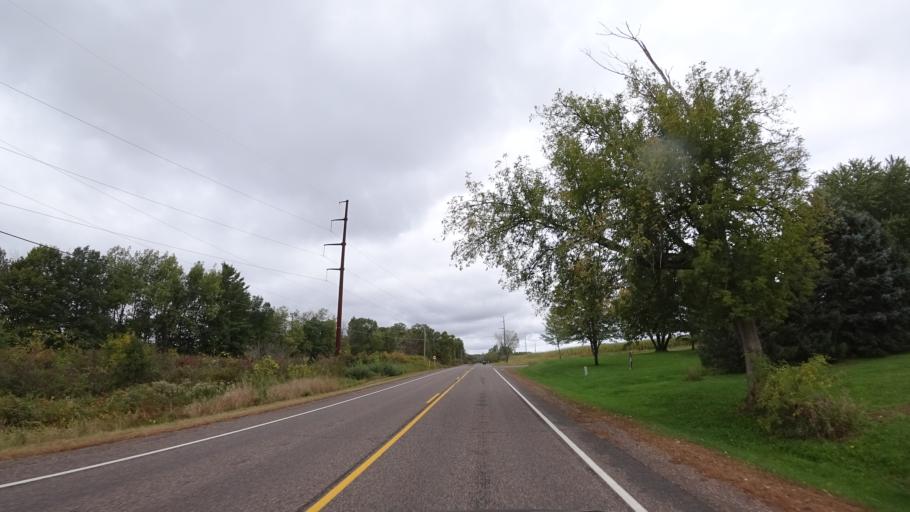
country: US
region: Wisconsin
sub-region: Chippewa County
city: Lake Wissota
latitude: 45.0232
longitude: -91.2869
